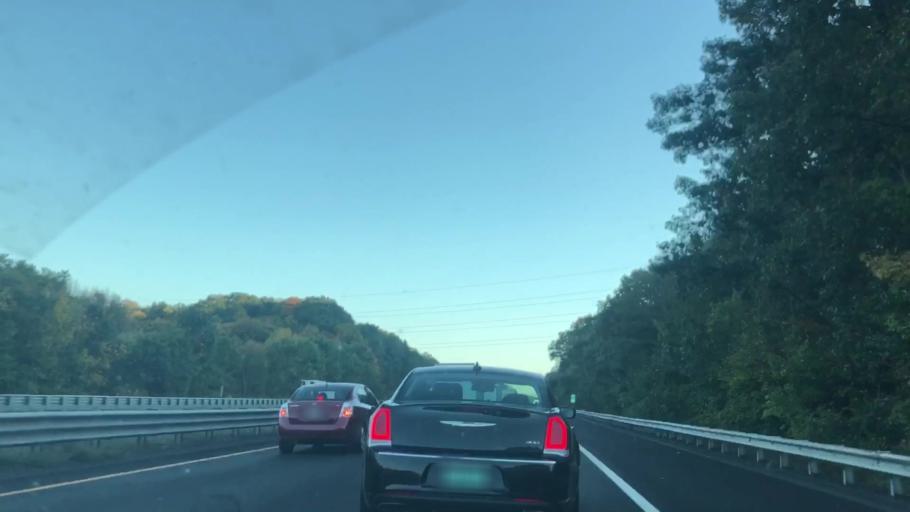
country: US
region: Massachusetts
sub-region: Franklin County
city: South Deerfield
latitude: 42.5151
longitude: -72.6236
